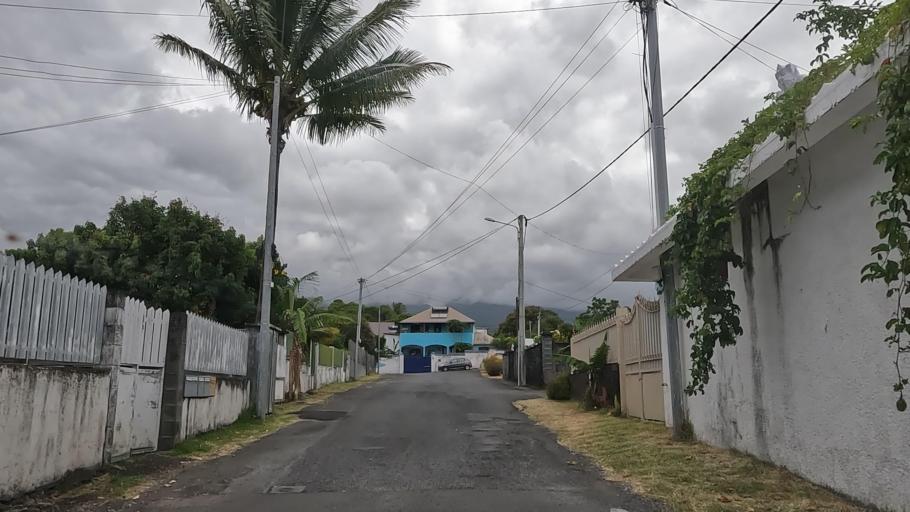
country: RE
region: Reunion
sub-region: Reunion
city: Saint-Benoit
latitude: -21.0892
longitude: 55.7462
